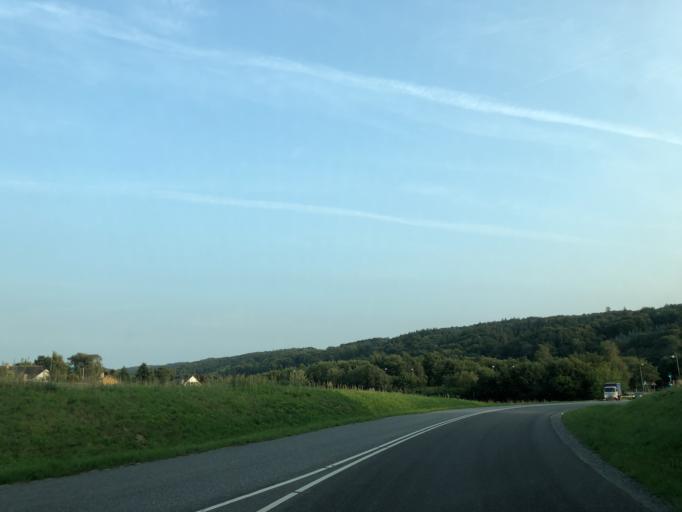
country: DK
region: South Denmark
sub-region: Vejle Kommune
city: Jelling
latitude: 55.7101
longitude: 9.4701
